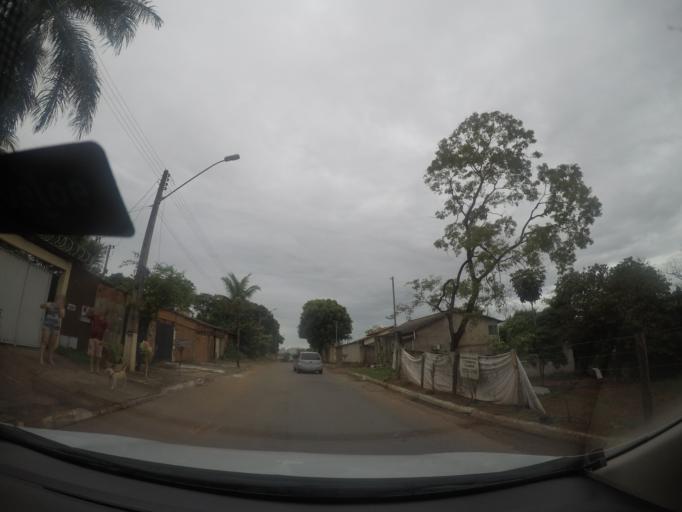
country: BR
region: Goias
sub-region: Goiania
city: Goiania
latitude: -16.6704
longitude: -49.3284
